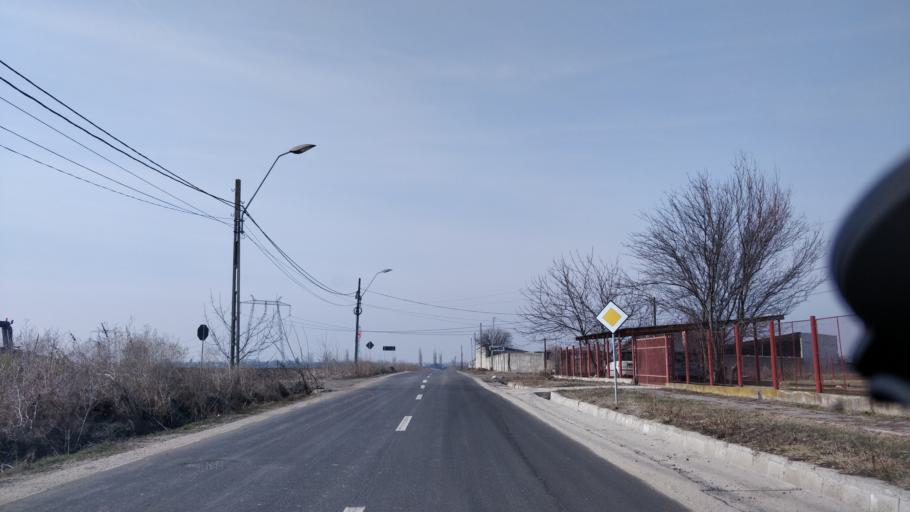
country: RO
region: Giurgiu
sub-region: Comuna Bolintin Deal
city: Bolintin Deal
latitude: 44.4622
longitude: 25.8030
